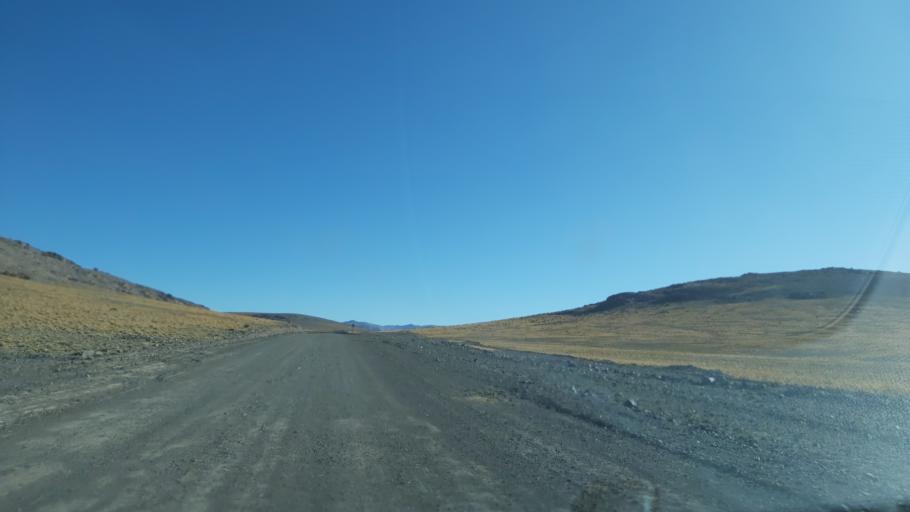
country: CL
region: Atacama
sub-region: Provincia de Chanaral
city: Diego de Almagro
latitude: -26.4635
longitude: -69.2936
